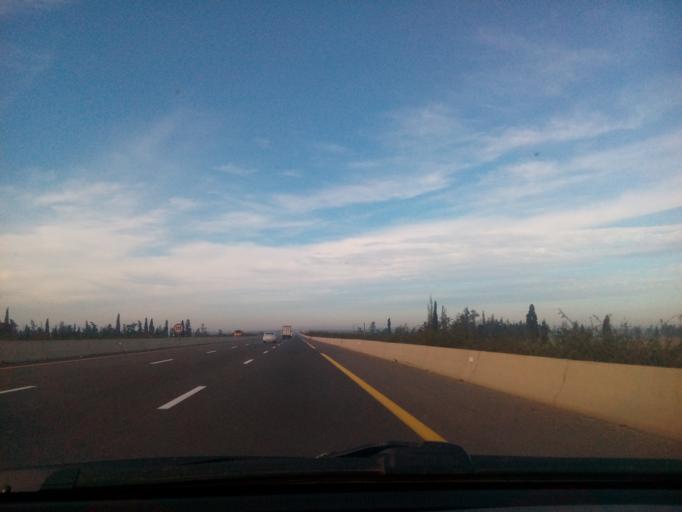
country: DZ
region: Mascara
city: Sig
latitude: 35.6172
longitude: 0.0225
